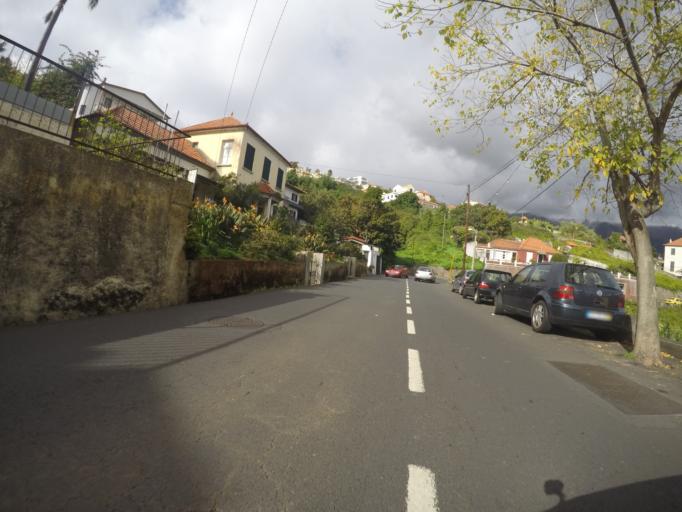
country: PT
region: Madeira
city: Camara de Lobos
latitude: 32.6613
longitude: -16.9442
